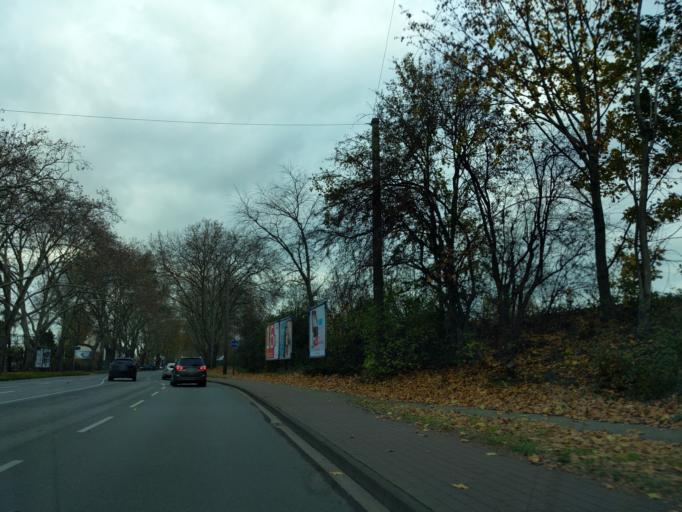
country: DE
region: North Rhine-Westphalia
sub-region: Regierungsbezirk Koln
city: Riehl
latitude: 50.9772
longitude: 6.9729
